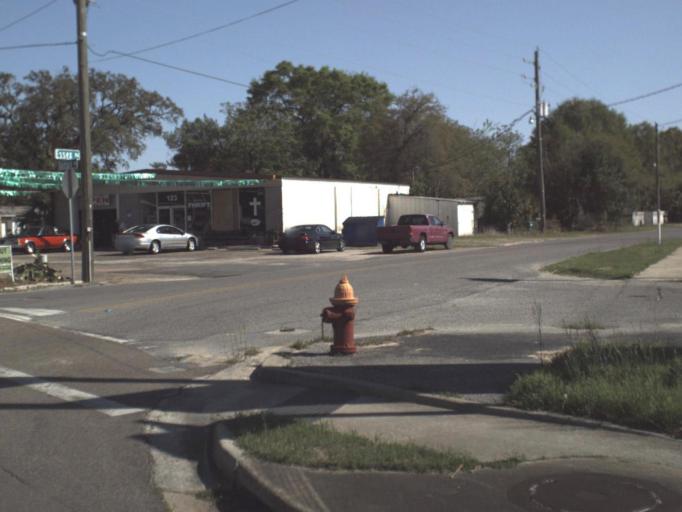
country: US
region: Florida
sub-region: Okaloosa County
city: Ocean City
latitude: 30.4469
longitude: -86.6091
